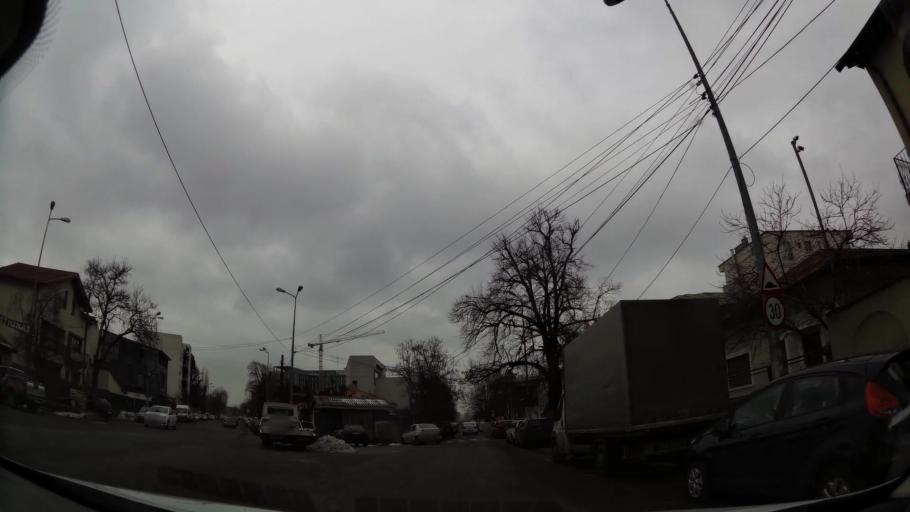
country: RO
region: Ilfov
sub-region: Comuna Chiajna
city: Rosu
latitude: 44.4708
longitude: 26.0584
